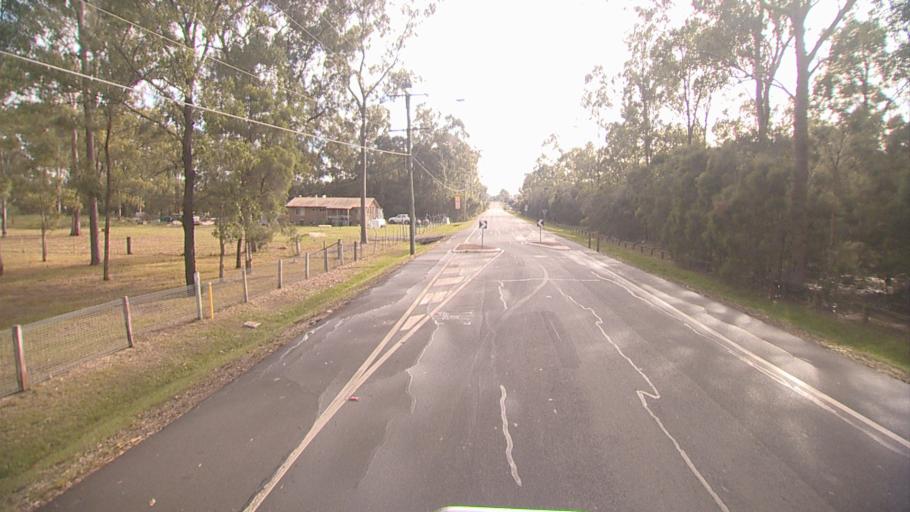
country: AU
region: Queensland
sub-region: Logan
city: Waterford West
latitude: -27.6898
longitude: 153.1118
